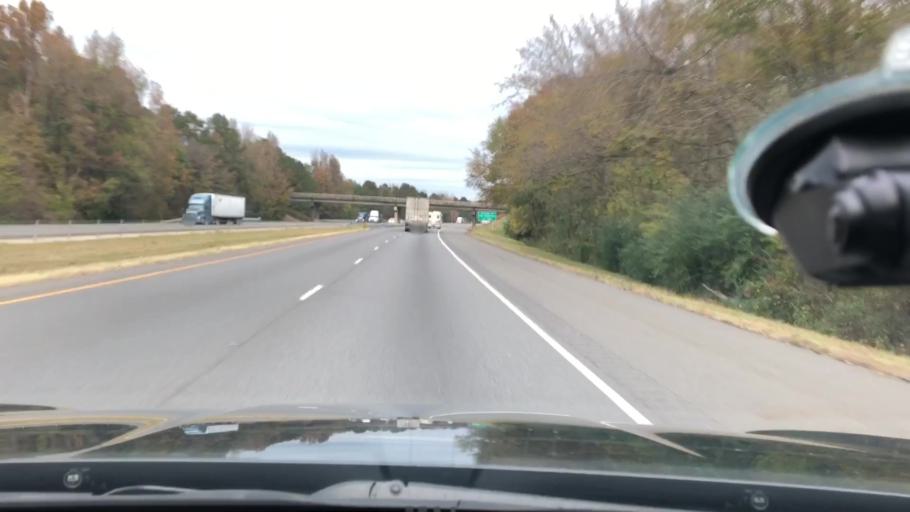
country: US
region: Arkansas
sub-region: Hot Spring County
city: Malvern
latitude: 34.3843
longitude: -92.8470
